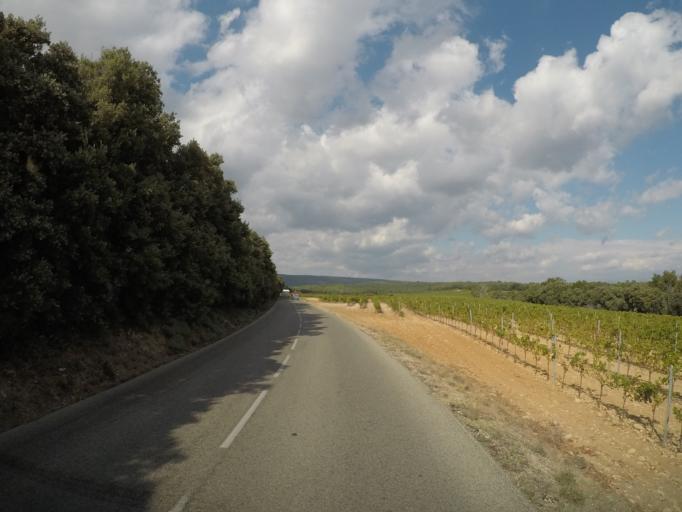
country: FR
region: Rhone-Alpes
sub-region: Departement de la Drome
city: Suze-la-Rousse
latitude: 44.3201
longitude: 4.8256
